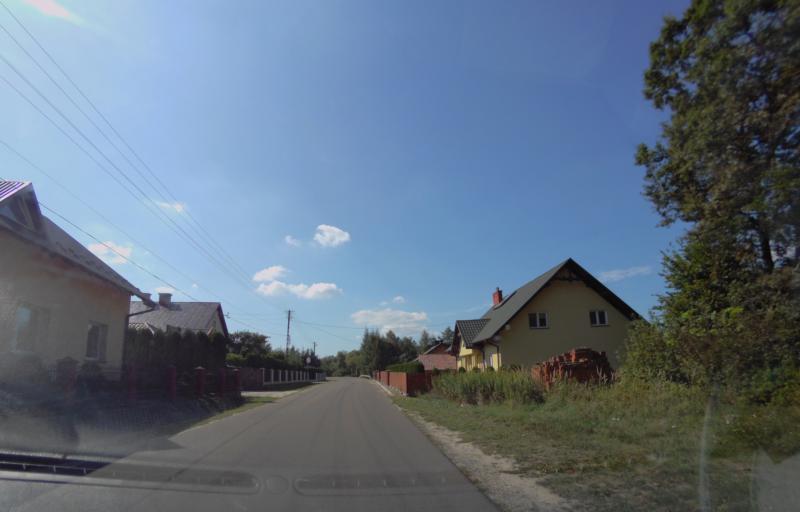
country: PL
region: Subcarpathian Voivodeship
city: Nowa Sarzyna
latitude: 50.3056
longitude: 22.3203
